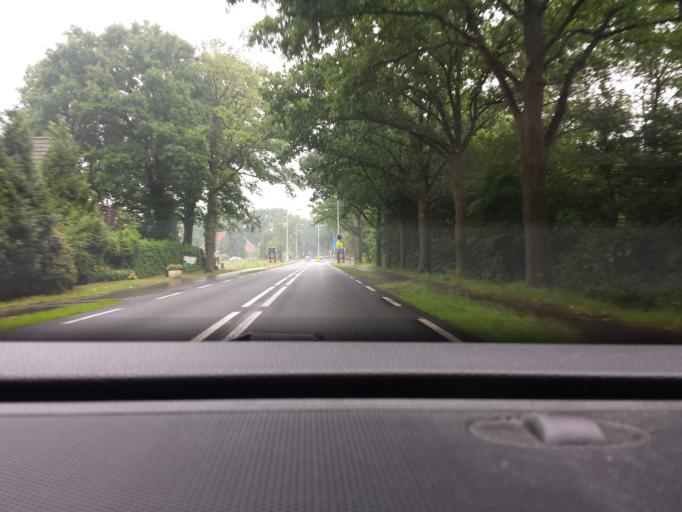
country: NL
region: Overijssel
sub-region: Gemeente Enschede
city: Enschede
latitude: 52.2001
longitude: 6.8314
